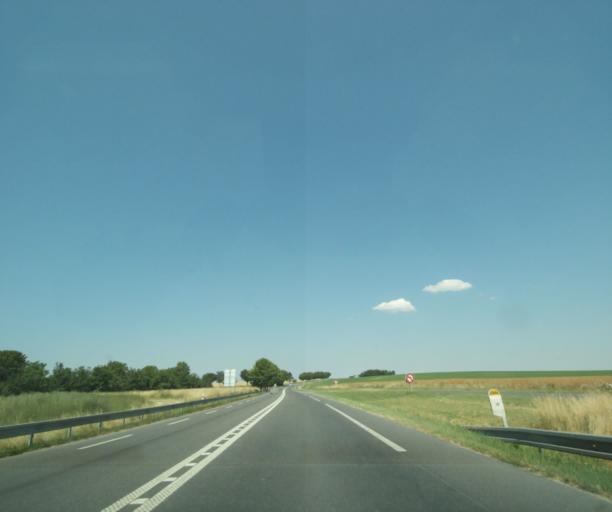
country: FR
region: Champagne-Ardenne
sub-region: Departement de la Marne
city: Verzy
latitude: 49.1408
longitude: 4.2252
